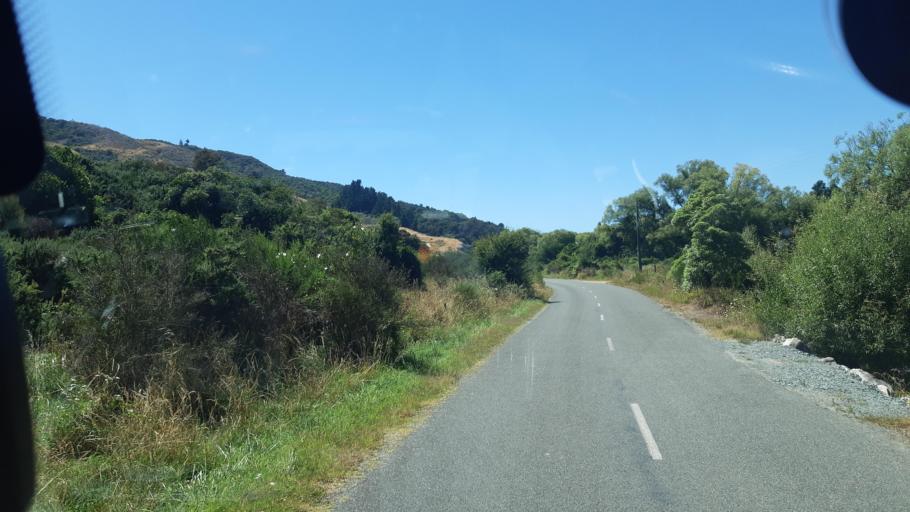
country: NZ
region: Tasman
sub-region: Tasman District
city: Motueka
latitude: -41.0506
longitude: 172.9519
